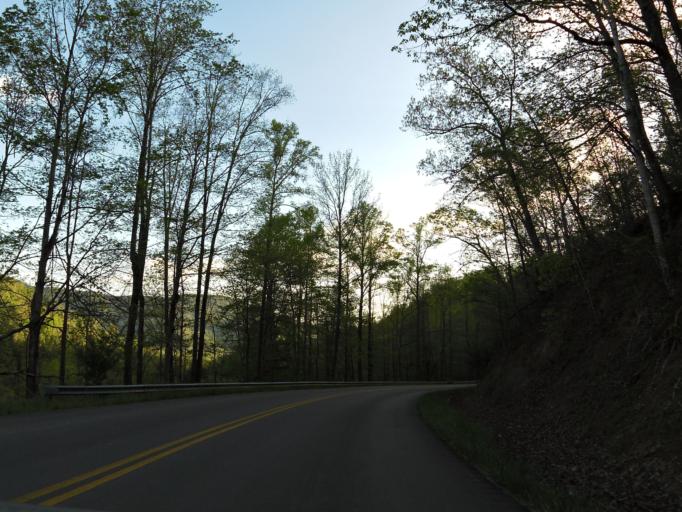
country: US
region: Kentucky
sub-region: Bell County
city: Middlesboro
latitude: 36.6068
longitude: -83.8794
